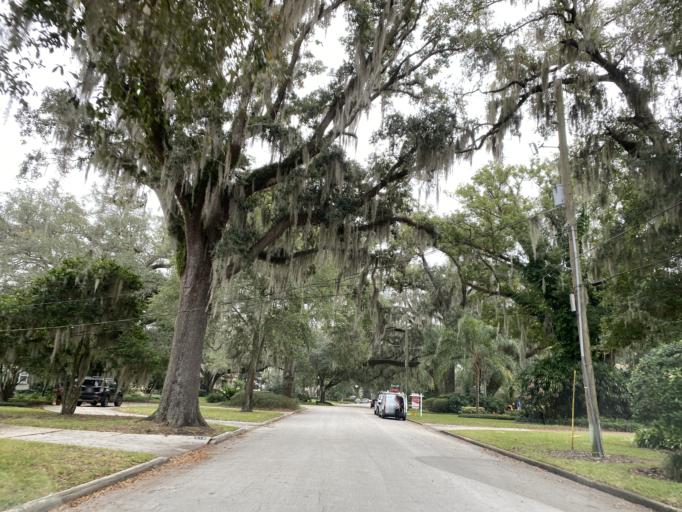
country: US
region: Florida
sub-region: Orange County
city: Orlando
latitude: 28.5559
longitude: -81.3925
